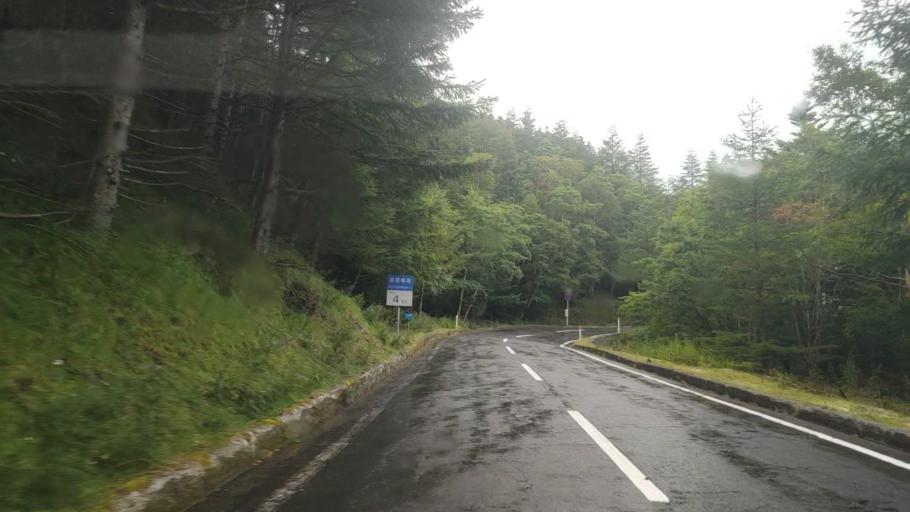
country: JP
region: Shizuoka
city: Fujinomiya
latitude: 35.3299
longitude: 138.7315
